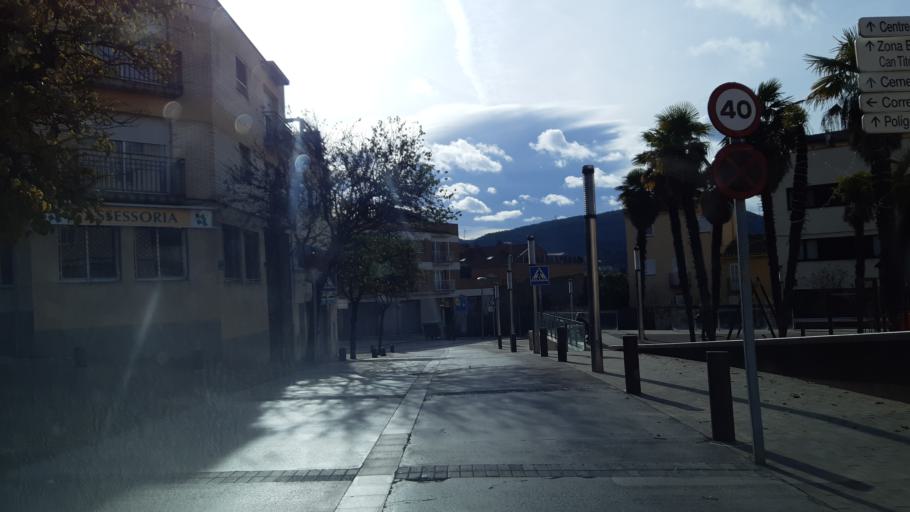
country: ES
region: Catalonia
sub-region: Provincia de Barcelona
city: Vilanova del Cami
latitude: 41.5714
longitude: 1.6356
